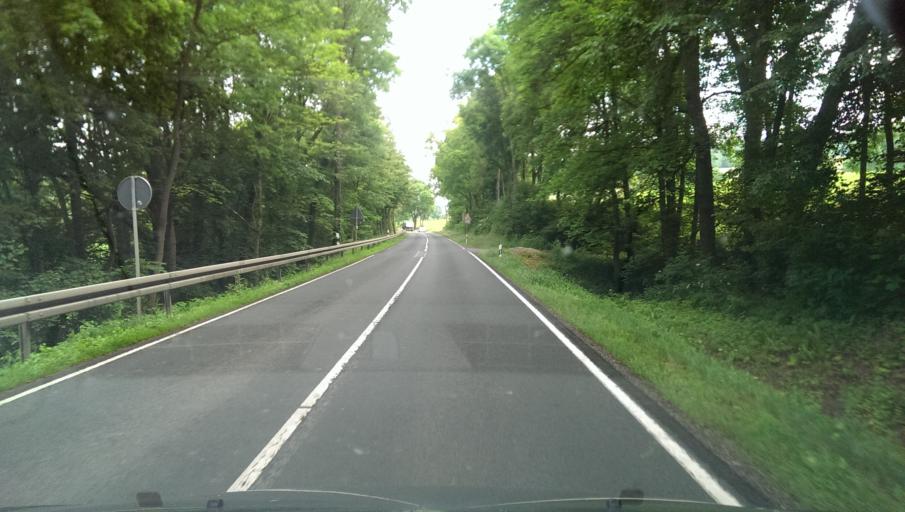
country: DE
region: Thuringia
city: Barchfeld
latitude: 50.8182
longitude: 11.1824
